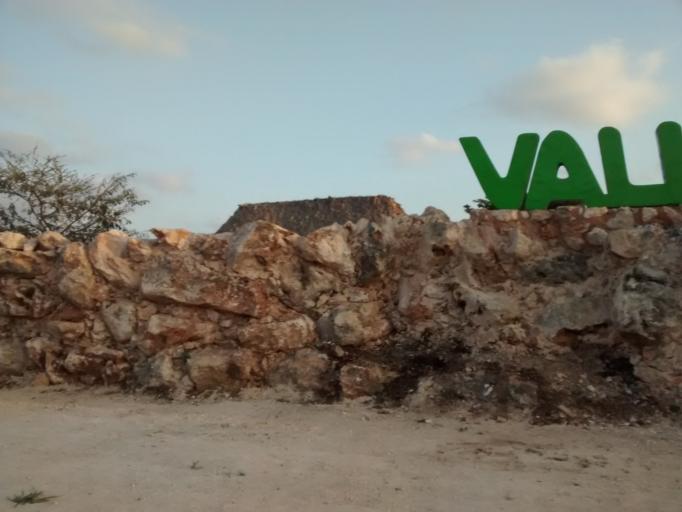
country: MX
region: Yucatan
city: Valladolid
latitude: 20.7251
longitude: -88.2075
